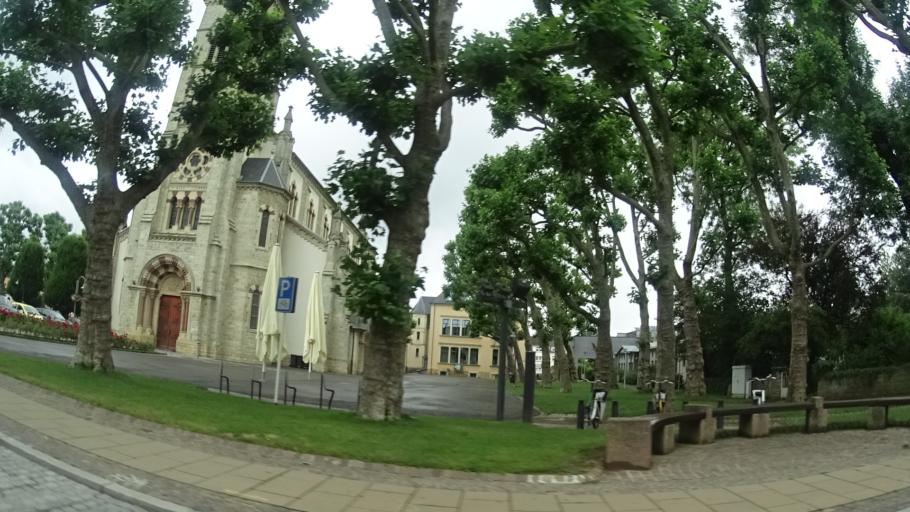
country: LU
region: Luxembourg
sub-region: Canton d'Esch-sur-Alzette
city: Bettembourg
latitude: 49.5188
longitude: 6.0987
